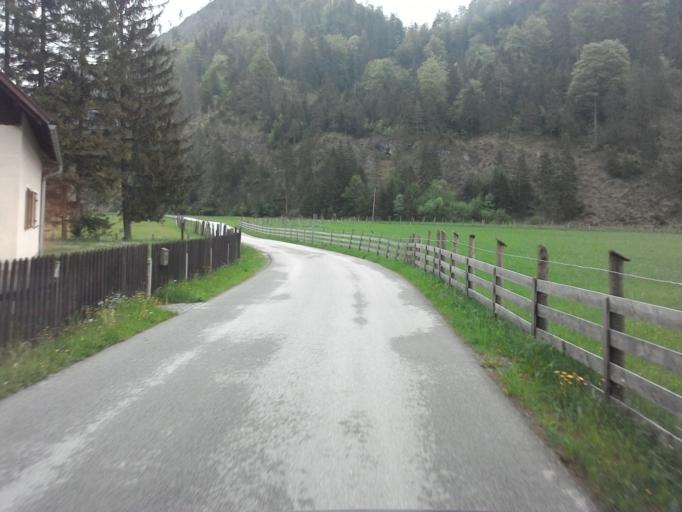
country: AT
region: Styria
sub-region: Politischer Bezirk Liezen
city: Wildalpen
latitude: 47.6774
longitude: 14.9901
